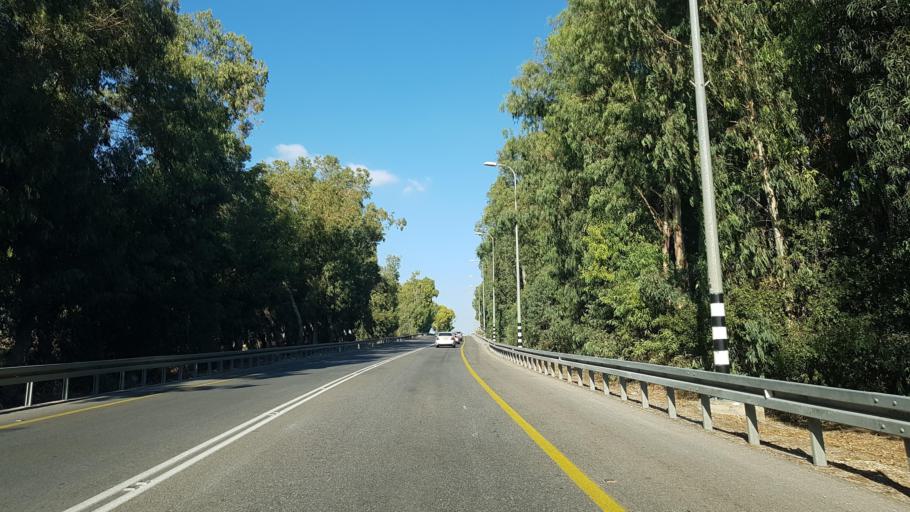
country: PS
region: West Bank
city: Zayta
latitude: 32.3555
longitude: 35.0156
